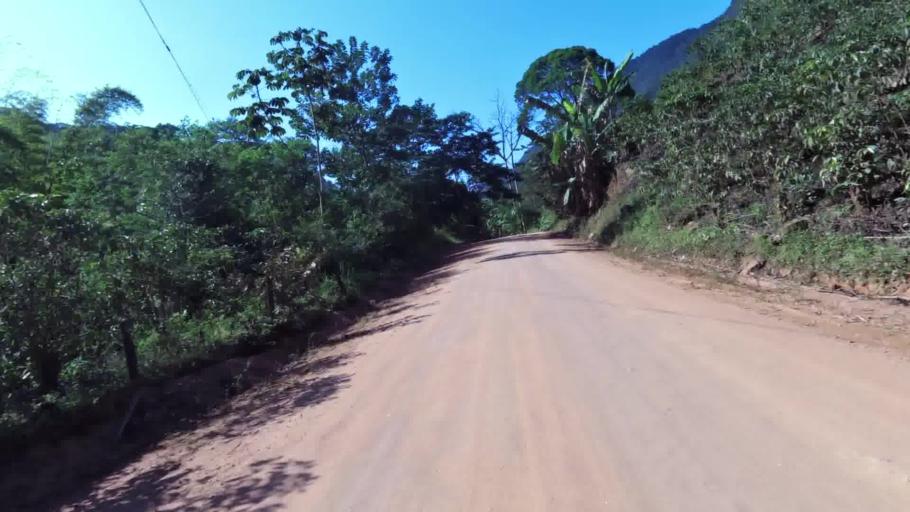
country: BR
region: Espirito Santo
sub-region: Alfredo Chaves
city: Alfredo Chaves
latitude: -20.5569
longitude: -40.7293
